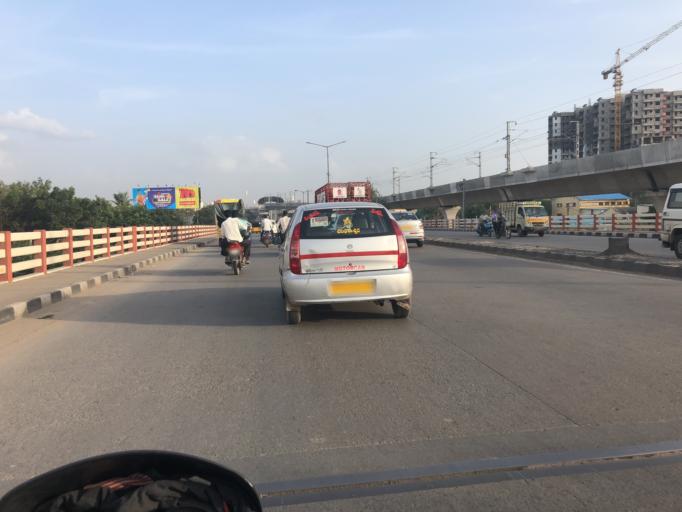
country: IN
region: Telangana
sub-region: Rangareddi
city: Kukatpalli
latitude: 17.4618
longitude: 78.4315
